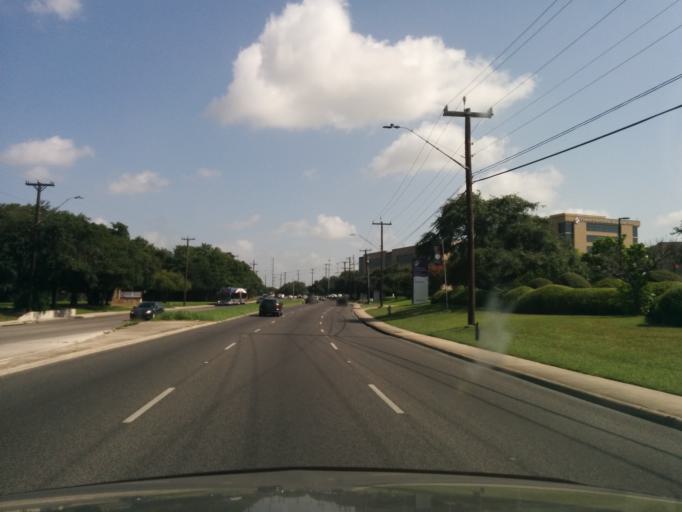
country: US
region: Texas
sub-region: Bexar County
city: Leon Valley
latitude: 29.5114
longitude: -98.5913
